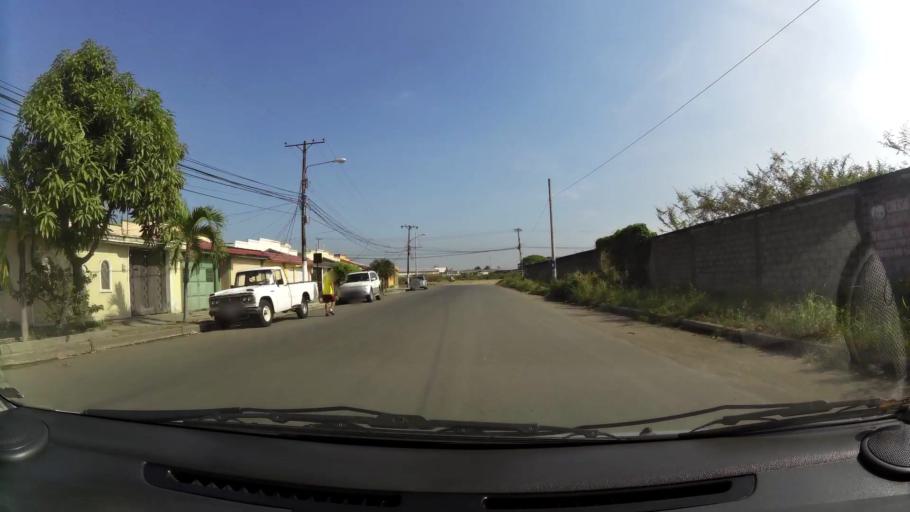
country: EC
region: Guayas
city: Eloy Alfaro
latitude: -2.1867
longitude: -79.8179
